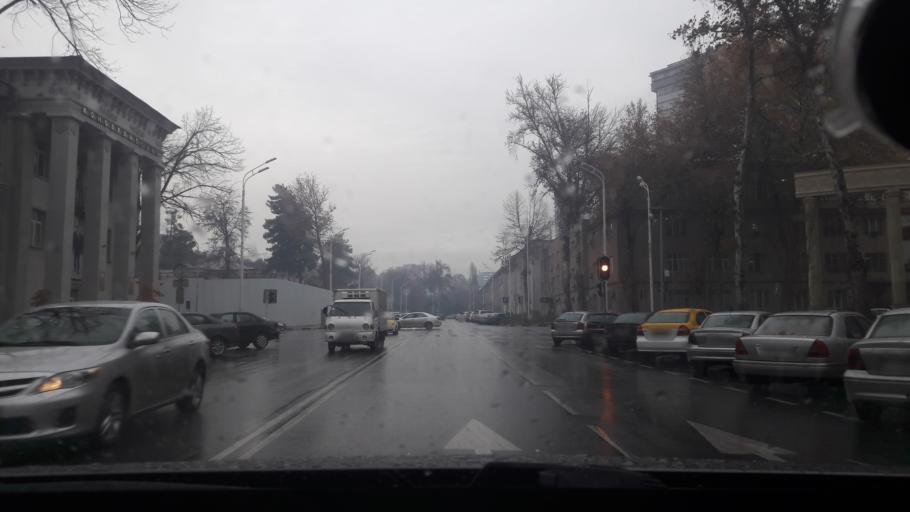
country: TJ
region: Dushanbe
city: Dushanbe
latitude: 38.5698
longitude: 68.7938
